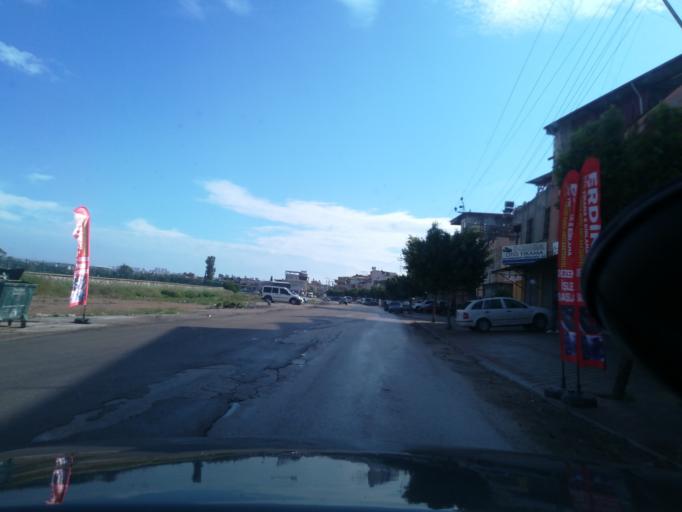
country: TR
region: Adana
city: Adana
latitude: 37.0144
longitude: 35.3609
